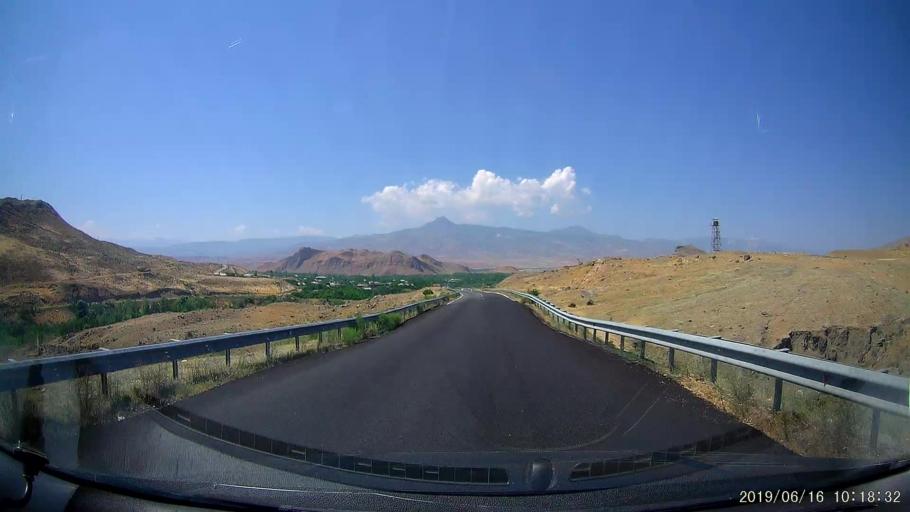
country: TR
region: Igdir
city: Tuzluca
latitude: 40.1594
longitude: 43.6668
